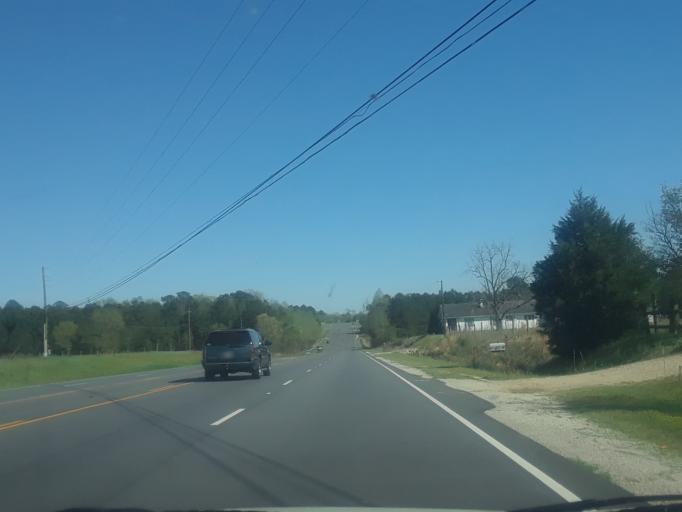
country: US
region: North Carolina
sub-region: Harnett County
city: Buies Creek
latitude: 35.3855
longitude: -78.7230
